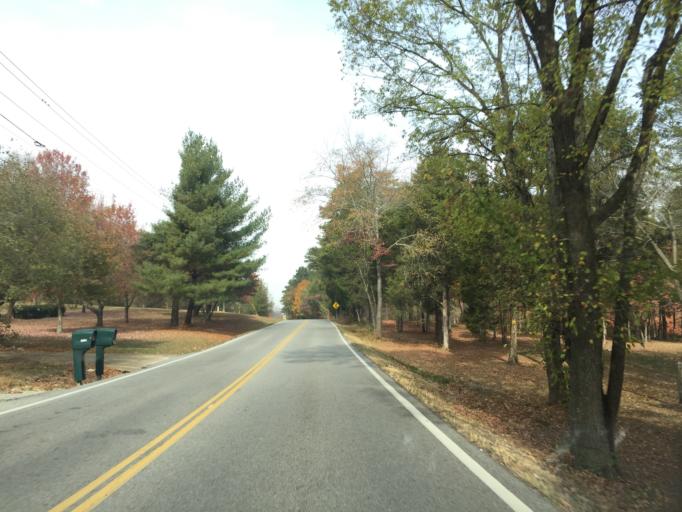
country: US
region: Tennessee
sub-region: Hamilton County
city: Collegedale
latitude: 35.1010
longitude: -85.0792
